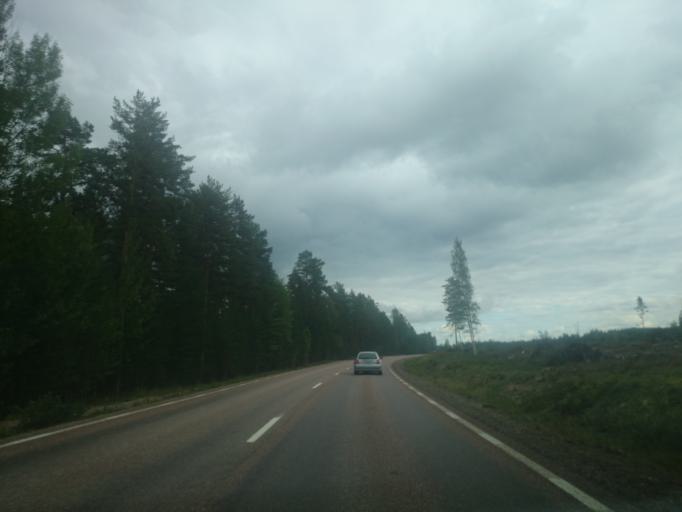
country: SE
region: Gaevleborg
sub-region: Ljusdals Kommun
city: Farila
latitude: 61.9433
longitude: 15.4638
